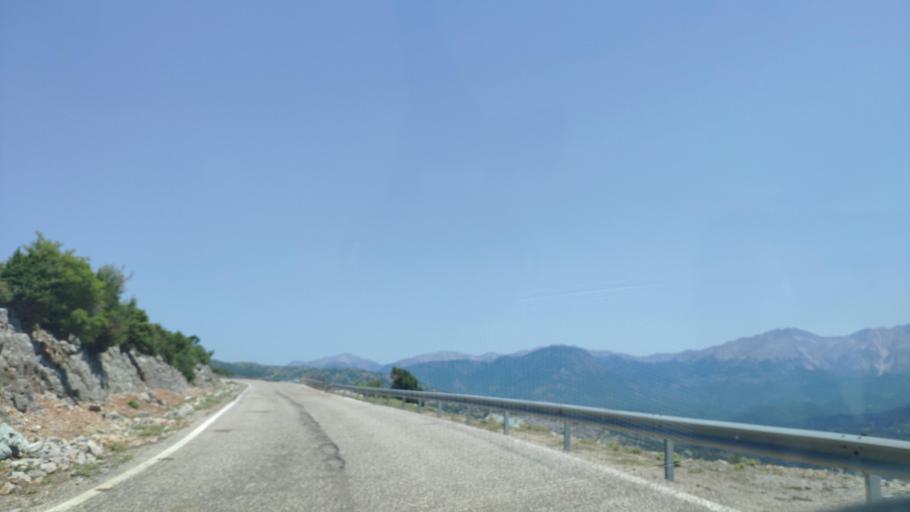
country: GR
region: West Greece
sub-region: Nomos Aitolias kai Akarnanias
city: Krikellos
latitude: 39.0523
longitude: 21.3833
